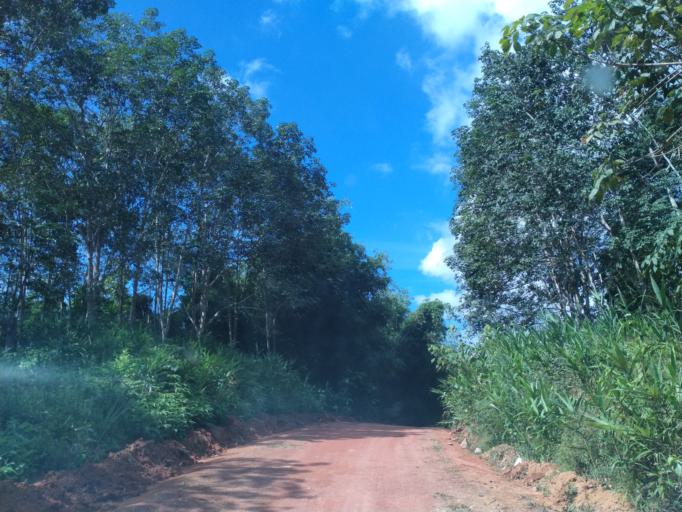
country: TH
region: Nong Khai
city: Rattanawapi
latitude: 18.6395
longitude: 102.9306
